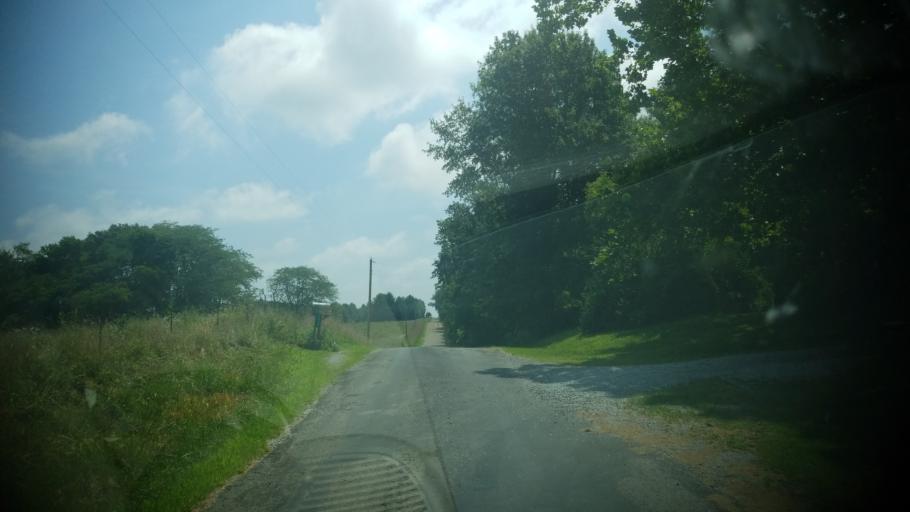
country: US
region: Illinois
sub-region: Wayne County
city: Fairfield
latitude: 38.5300
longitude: -88.3975
